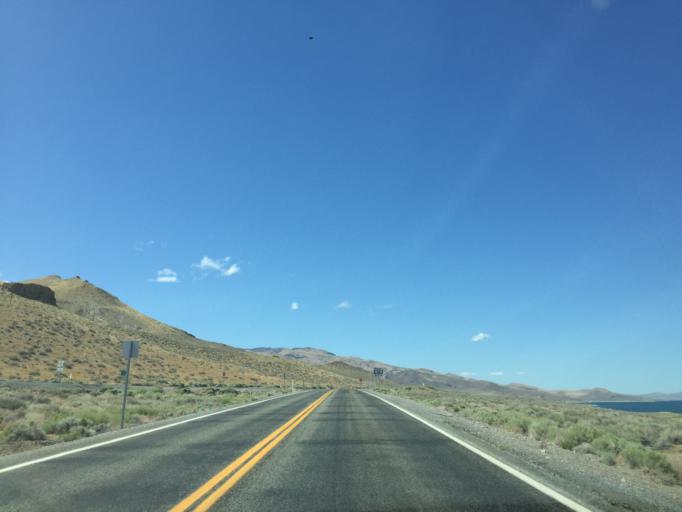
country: US
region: Nevada
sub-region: Washoe County
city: Spanish Springs
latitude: 39.9131
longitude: -119.5668
